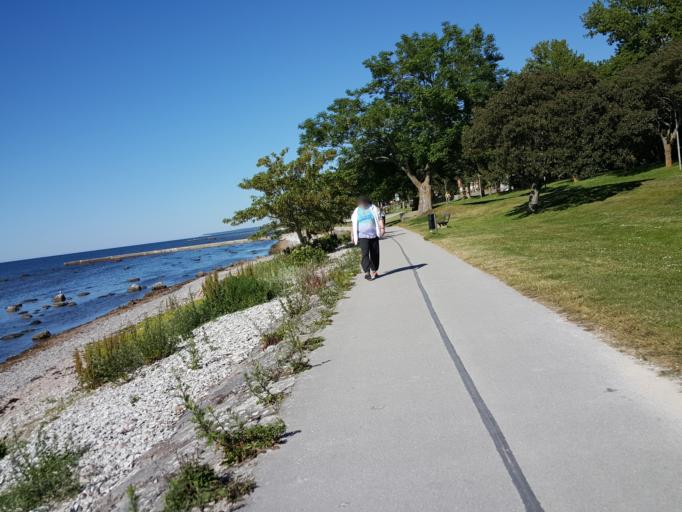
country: SE
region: Gotland
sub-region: Gotland
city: Visby
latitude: 57.6477
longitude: 18.2967
